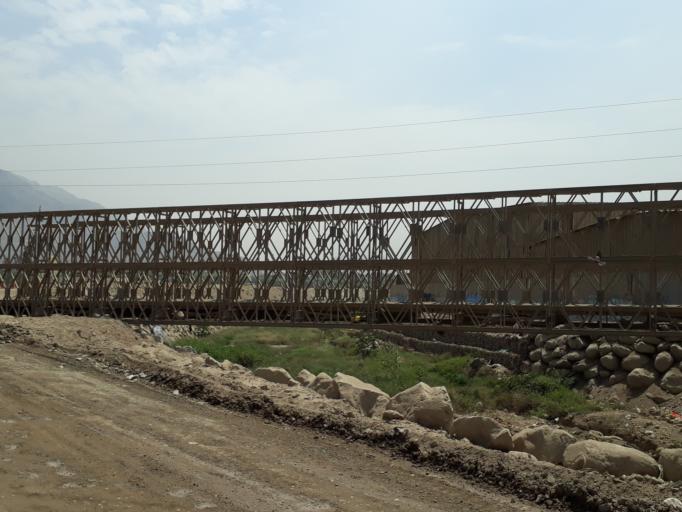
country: PE
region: Lima
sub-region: Lima
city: Santa Maria
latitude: -11.9992
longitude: -76.9163
